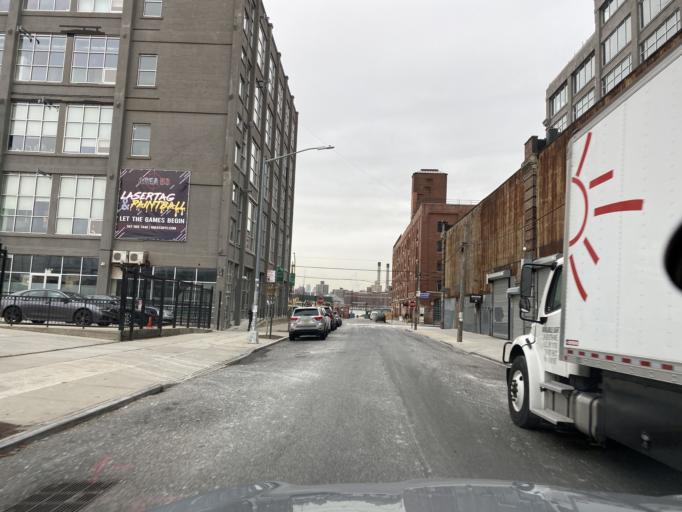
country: US
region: New York
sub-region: Queens County
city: Long Island City
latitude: 40.7284
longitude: -73.9582
